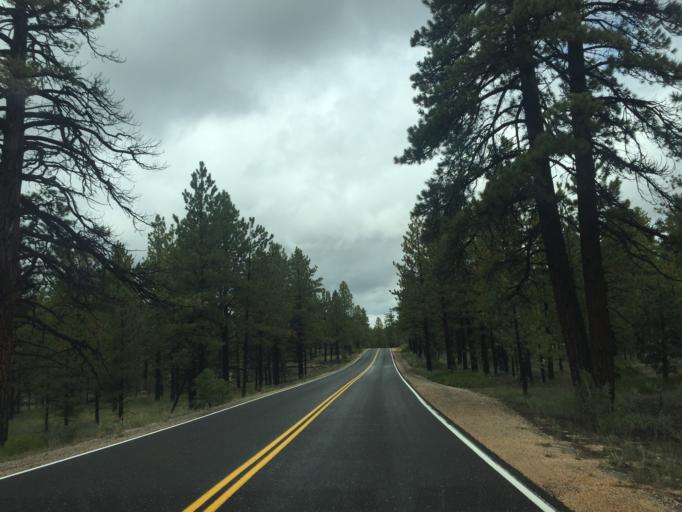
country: US
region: Utah
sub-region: Garfield County
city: Panguitch
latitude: 37.6119
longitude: -112.1746
